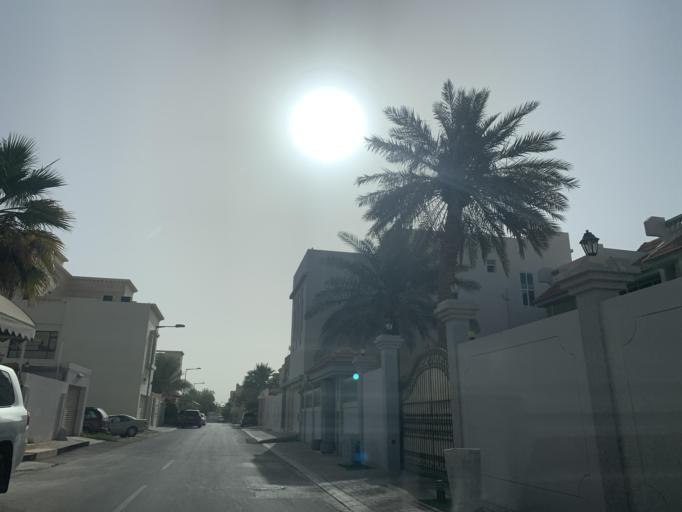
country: BH
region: Northern
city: Ar Rifa'
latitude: 26.1417
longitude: 50.5830
